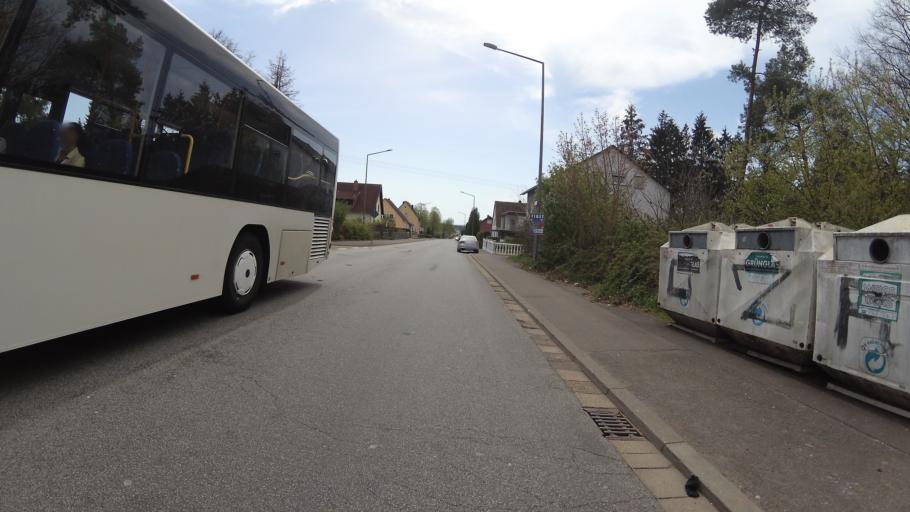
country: DE
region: Rheinland-Pfalz
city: Waldmohr
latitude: 49.3542
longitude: 7.3277
